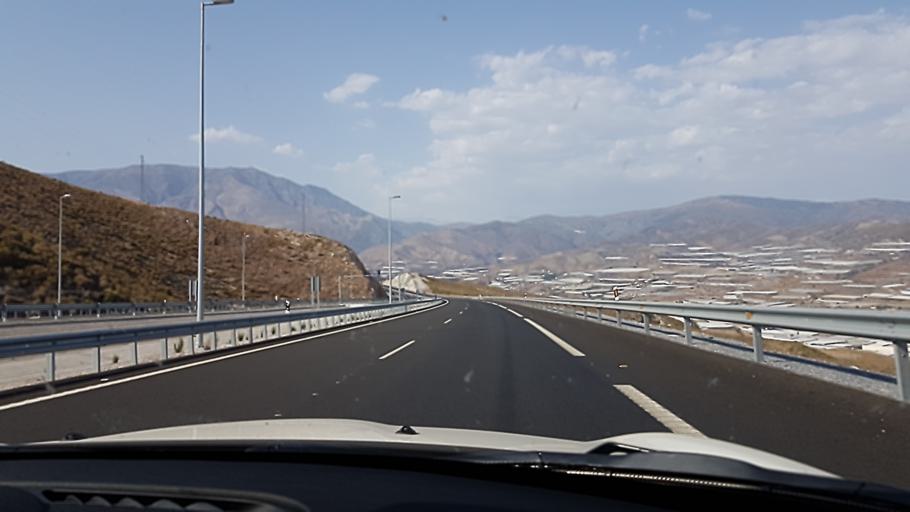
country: ES
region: Andalusia
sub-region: Provincia de Granada
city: Gualchos
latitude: 36.7241
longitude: -3.3751
